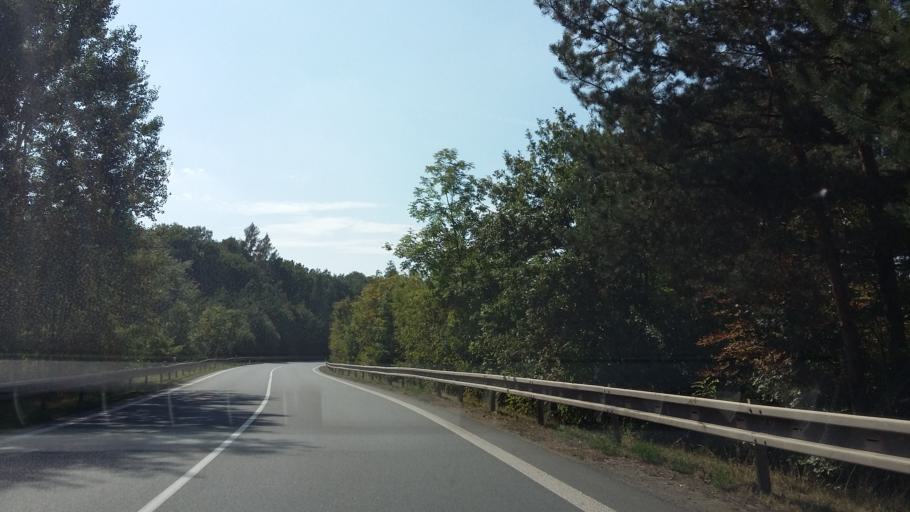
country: CZ
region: Central Bohemia
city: Libice nad Cidlinou
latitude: 50.1214
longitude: 15.1785
